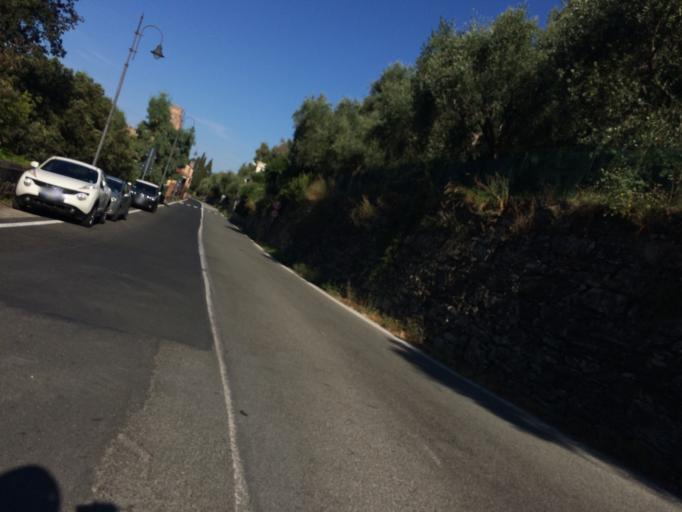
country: IT
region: Liguria
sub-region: Provincia di Genova
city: Zoagli
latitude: 44.3337
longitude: 9.2769
